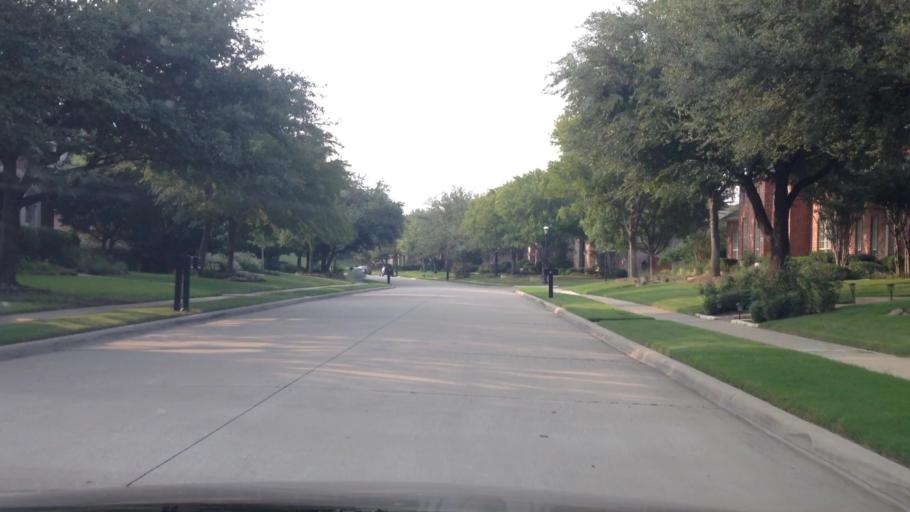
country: US
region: Texas
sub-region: Collin County
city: Frisco
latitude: 33.1263
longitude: -96.8400
